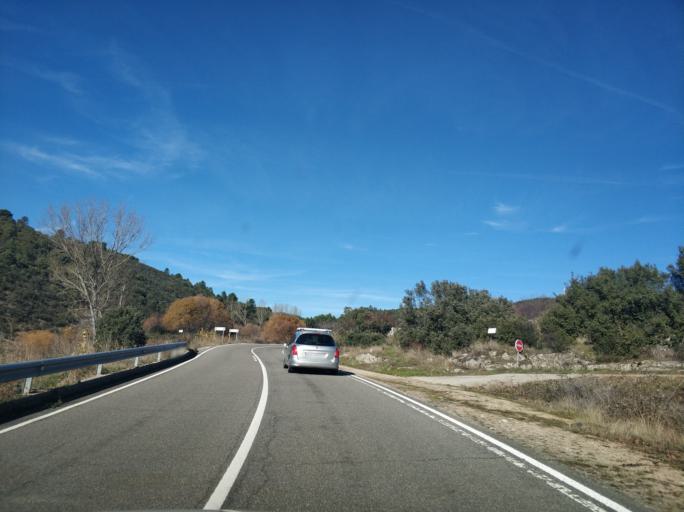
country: ES
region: Castille and Leon
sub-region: Provincia de Salamanca
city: San Esteban de la Sierra
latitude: 40.5225
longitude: -5.9128
